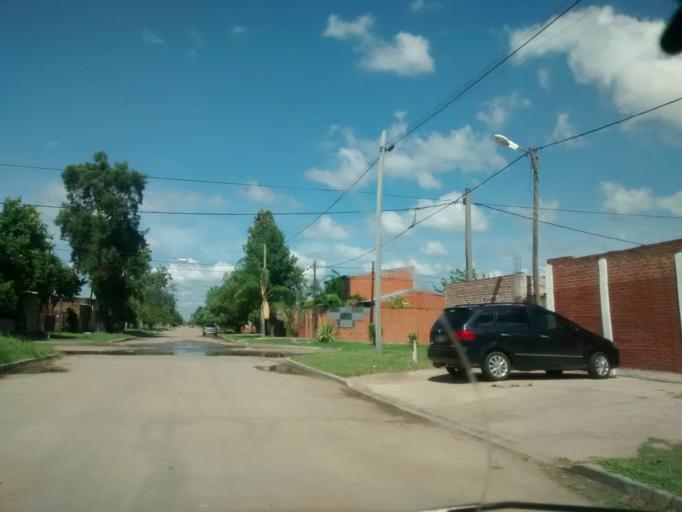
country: AR
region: Chaco
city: Resistencia
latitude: -27.4619
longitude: -59.0090
